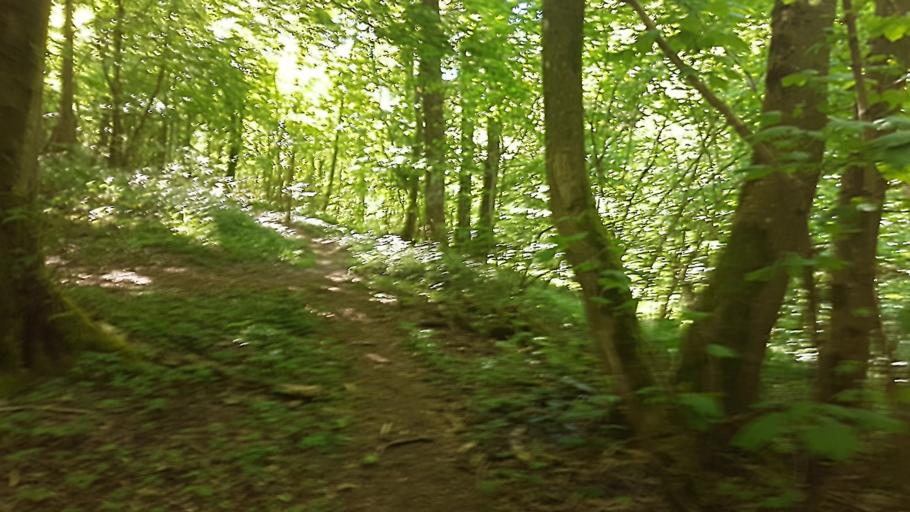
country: BE
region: Wallonia
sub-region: Province de Namur
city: Couvin
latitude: 50.0581
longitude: 4.5754
